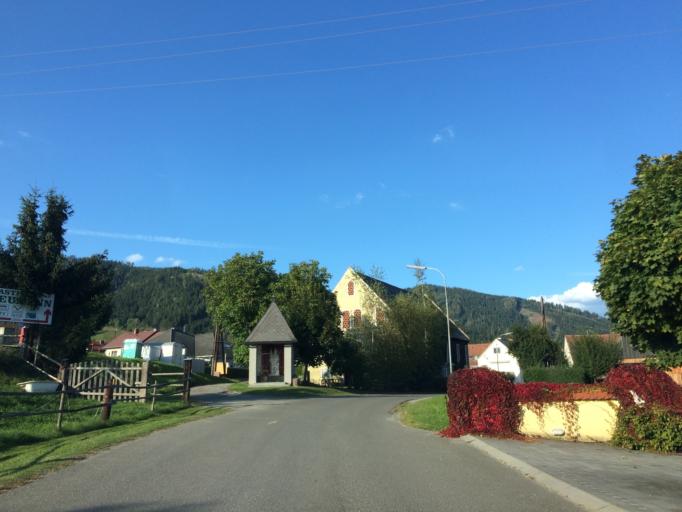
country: AT
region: Styria
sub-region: Politischer Bezirk Leoben
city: Kraubath an der Mur
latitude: 47.3043
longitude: 14.9364
